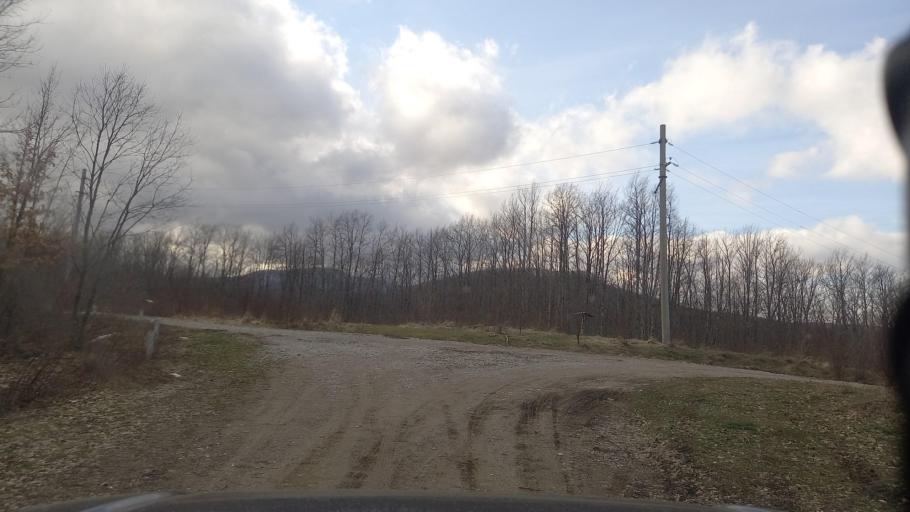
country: RU
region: Krasnodarskiy
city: Smolenskaya
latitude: 44.5750
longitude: 38.8022
